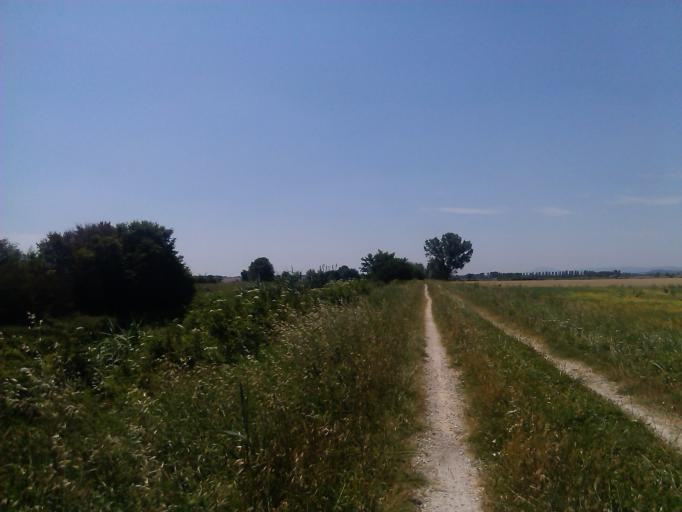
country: IT
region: Tuscany
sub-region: Province of Arezzo
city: Cesa
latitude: 43.3424
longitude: 11.8271
